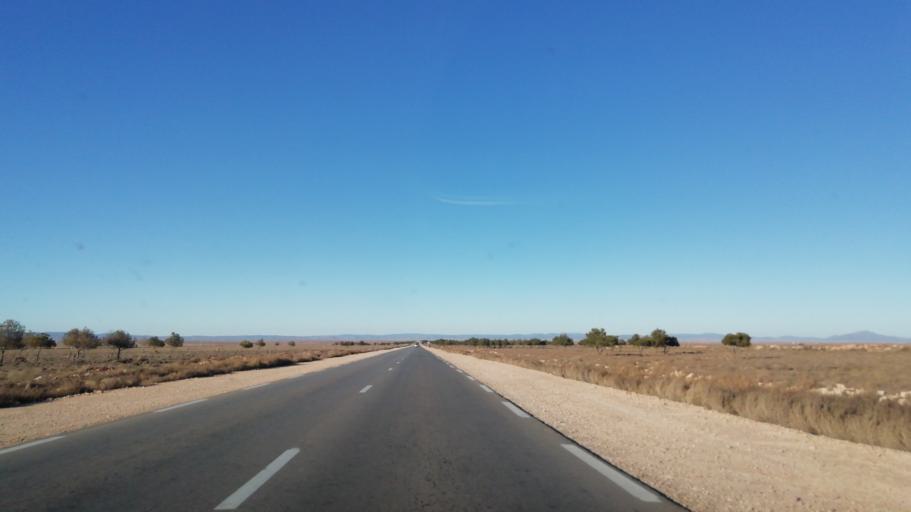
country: DZ
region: Tlemcen
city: Sebdou
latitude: 34.3294
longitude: -1.2641
